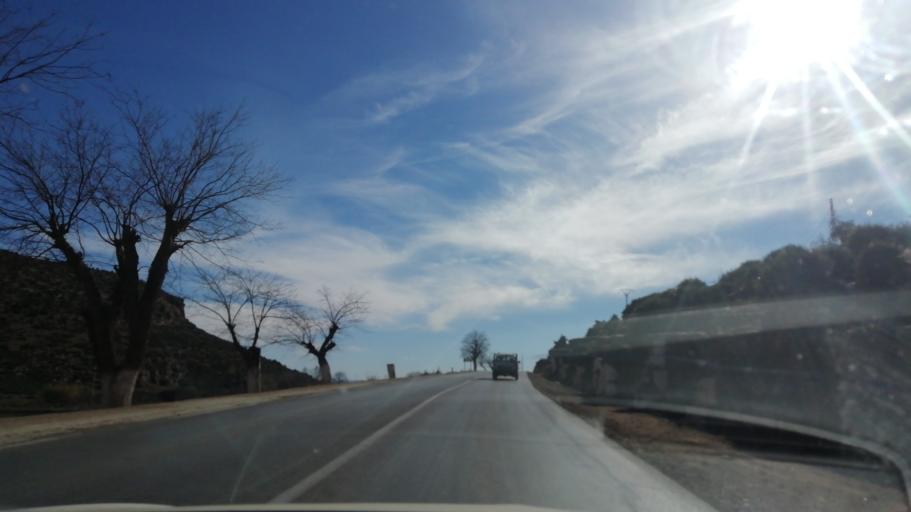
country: DZ
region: Tlemcen
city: Sebdou
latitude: 34.6963
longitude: -1.3126
